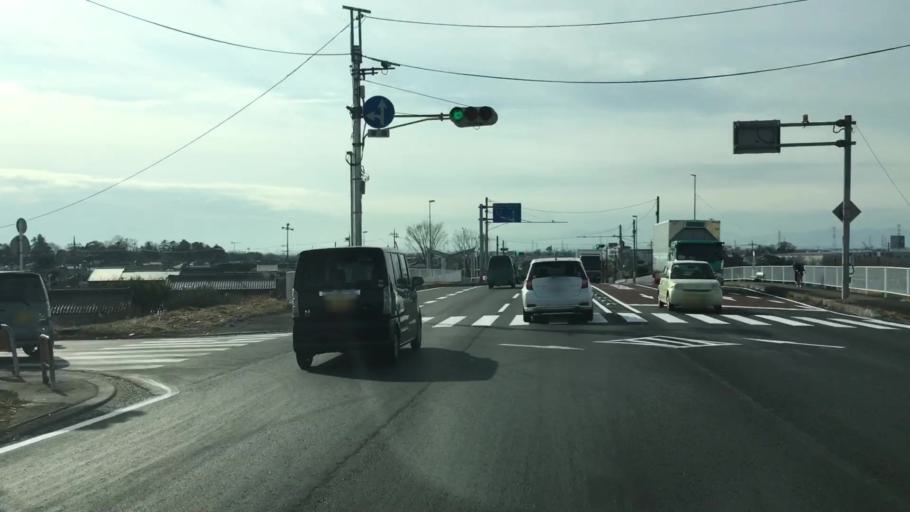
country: JP
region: Saitama
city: Menuma
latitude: 36.2359
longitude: 139.3758
